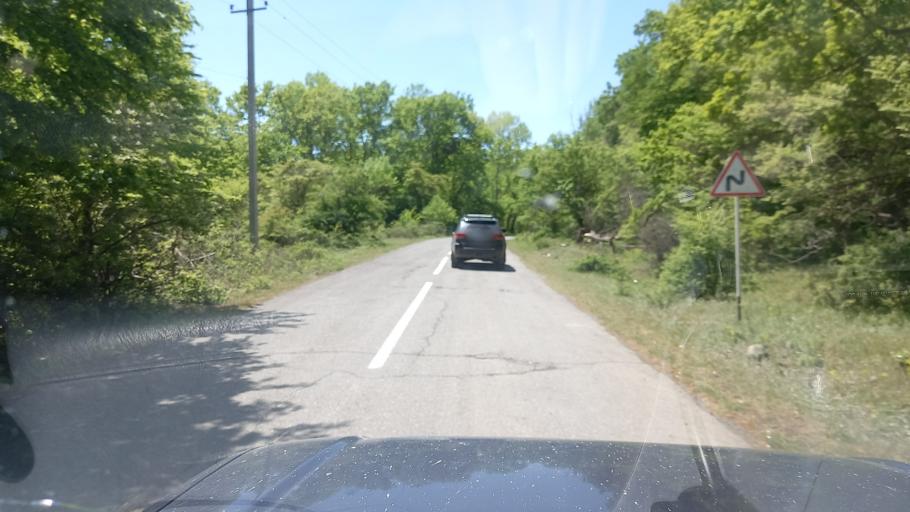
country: RU
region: Dagestan
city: Samur
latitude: 41.8416
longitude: 48.5734
